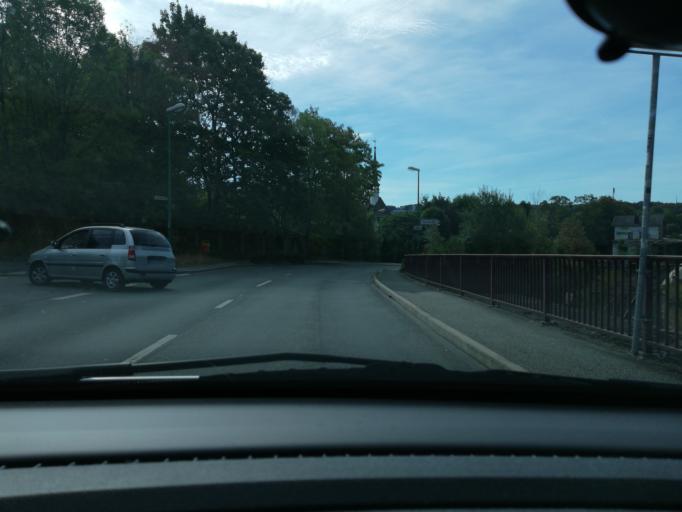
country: DE
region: North Rhine-Westphalia
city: Gevelsberg
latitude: 51.3063
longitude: 7.3434
